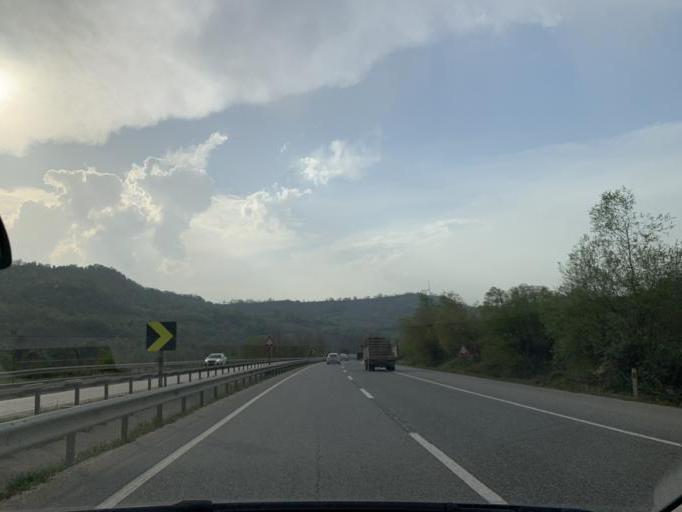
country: TR
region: Bursa
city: Tahtakopru
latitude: 39.9571
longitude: 29.6623
